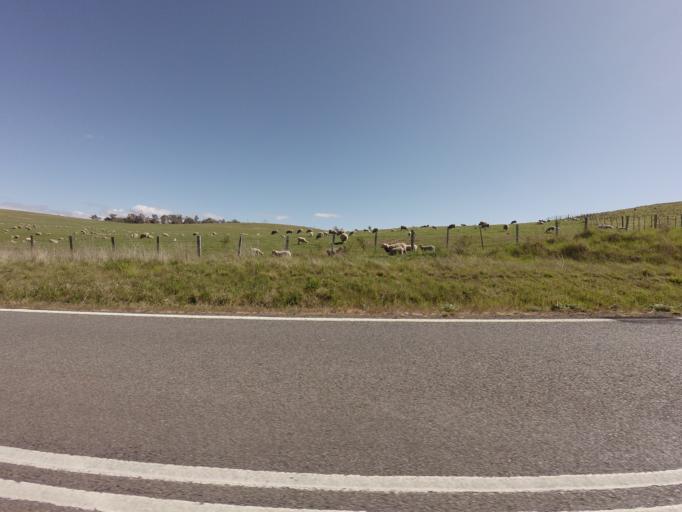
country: AU
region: Tasmania
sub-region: Derwent Valley
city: New Norfolk
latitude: -42.6429
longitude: 146.9200
